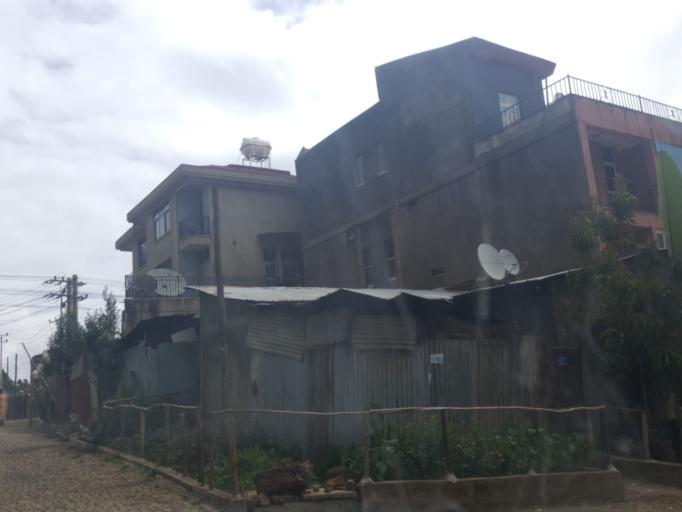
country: ET
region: Adis Abeba
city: Addis Ababa
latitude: 9.0688
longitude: 38.7406
